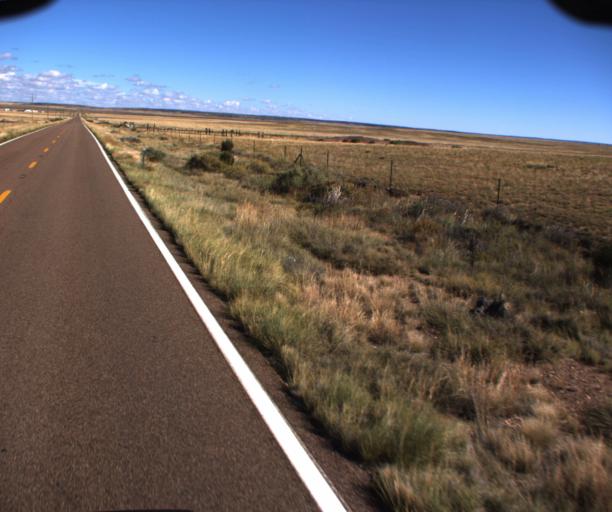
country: US
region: Arizona
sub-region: Apache County
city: Saint Johns
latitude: 34.5840
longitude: -109.3317
